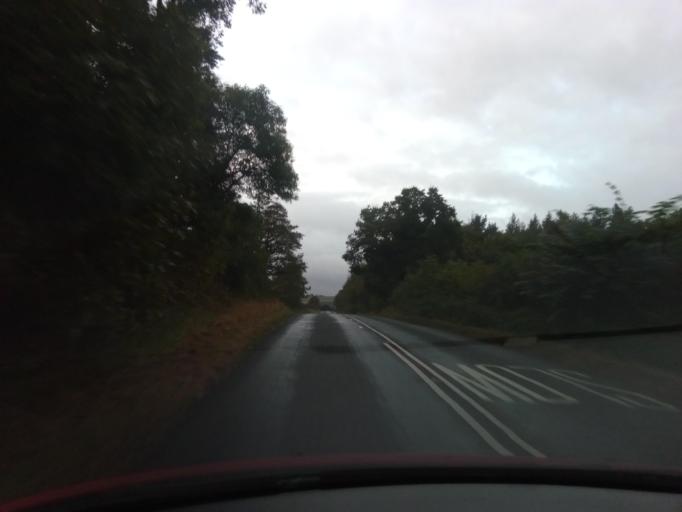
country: GB
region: England
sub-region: Darlington
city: Summerhouse
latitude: 54.5750
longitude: -1.6778
